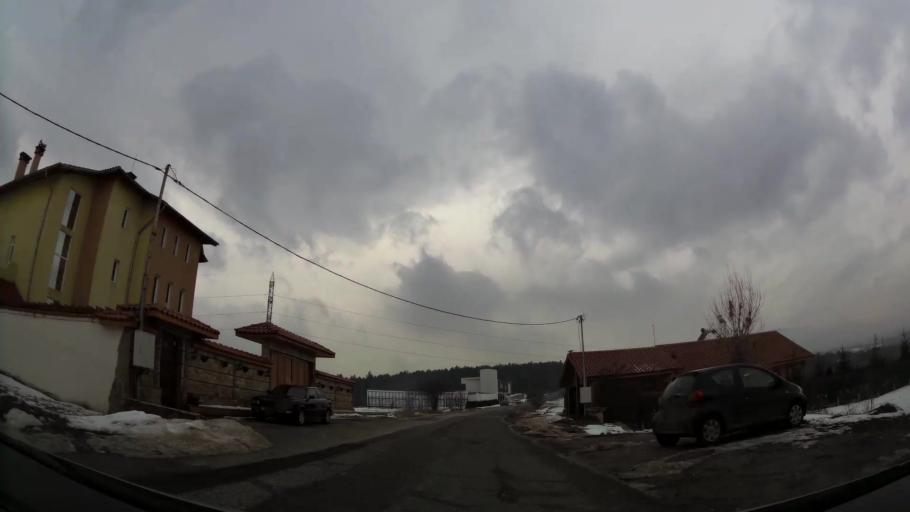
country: BG
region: Sofiya
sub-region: Obshtina Bozhurishte
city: Bozhurishte
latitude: 42.6670
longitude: 23.2184
